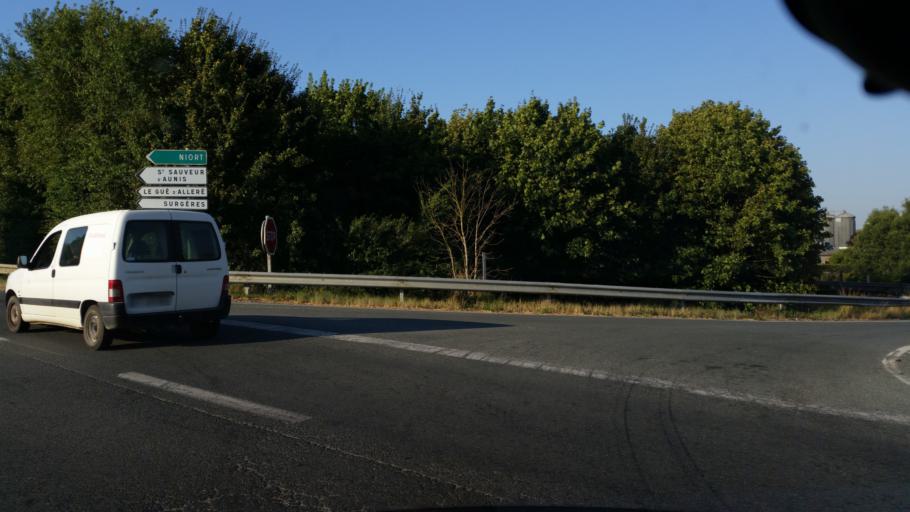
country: FR
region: Poitou-Charentes
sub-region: Departement de la Charente-Maritime
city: Saint-Jean-de-Liversay
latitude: 46.2287
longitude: -0.8793
